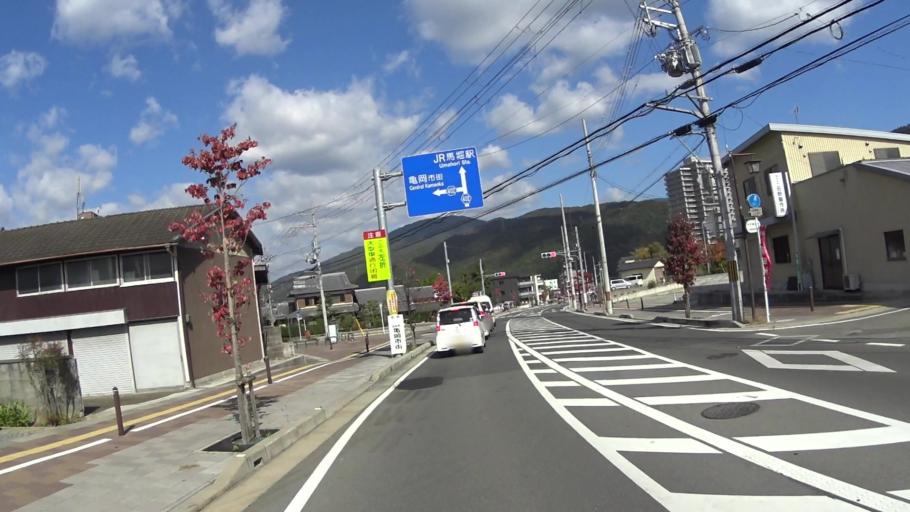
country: JP
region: Kyoto
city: Kameoka
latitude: 35.0071
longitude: 135.6023
